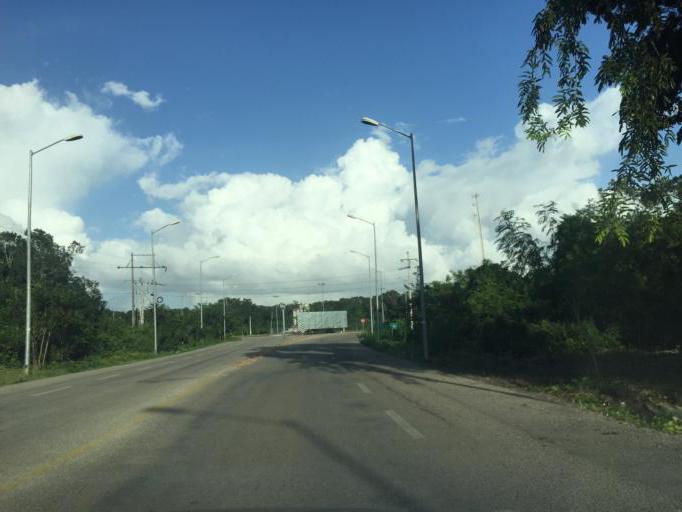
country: MX
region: Quintana Roo
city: Coba
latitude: 20.5071
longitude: -87.7198
